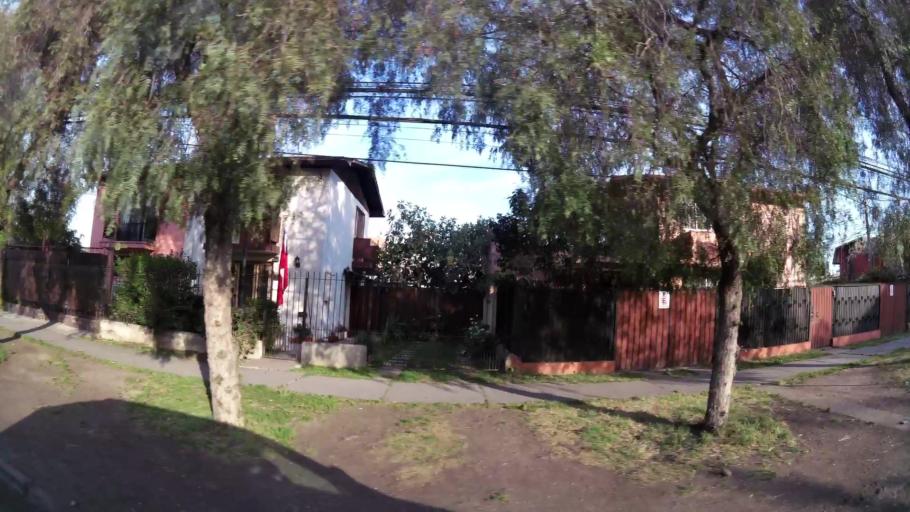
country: CL
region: Santiago Metropolitan
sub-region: Provincia de Santiago
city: La Pintana
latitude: -33.5349
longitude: -70.6669
